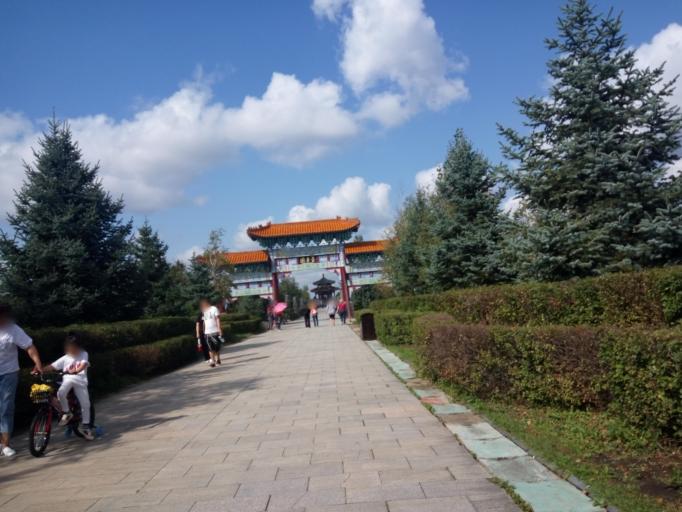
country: CN
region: Heilongjiang Sheng
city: Erjing
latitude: 48.6506
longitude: 126.1488
